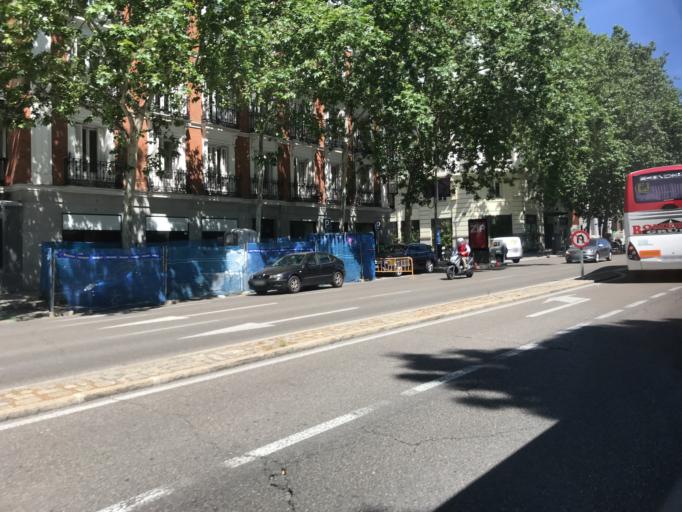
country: ES
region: Madrid
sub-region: Provincia de Madrid
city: Retiro
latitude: 40.4142
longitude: -3.6888
